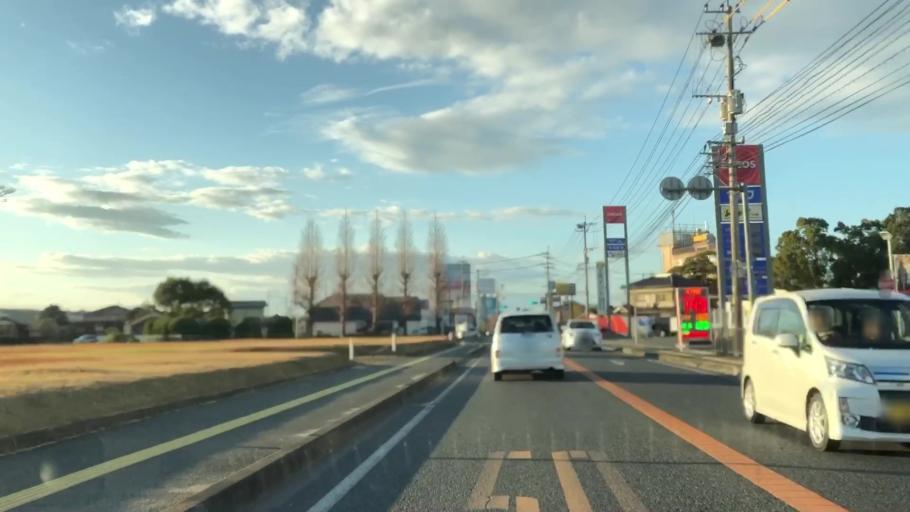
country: JP
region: Oita
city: Bungo-Takada-shi
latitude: 33.5280
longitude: 131.3398
